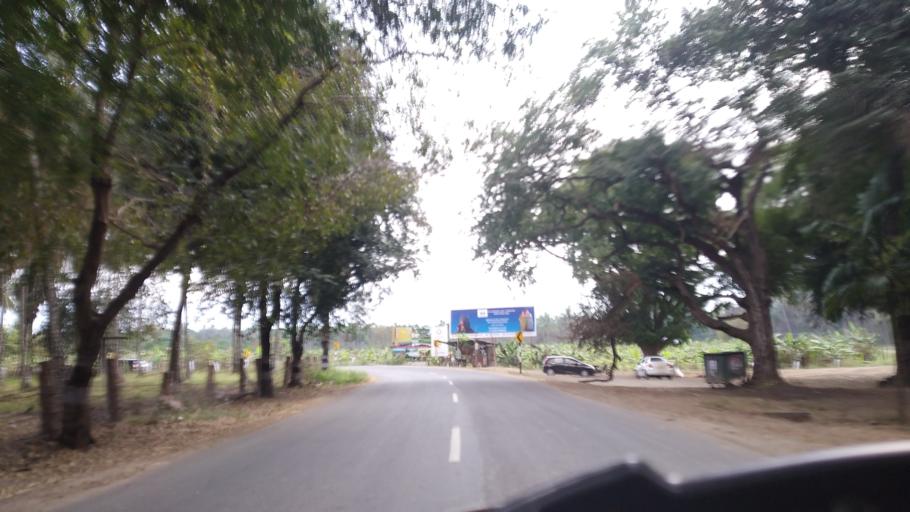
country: IN
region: Tamil Nadu
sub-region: Coimbatore
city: Perur
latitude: 10.9596
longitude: 76.7496
